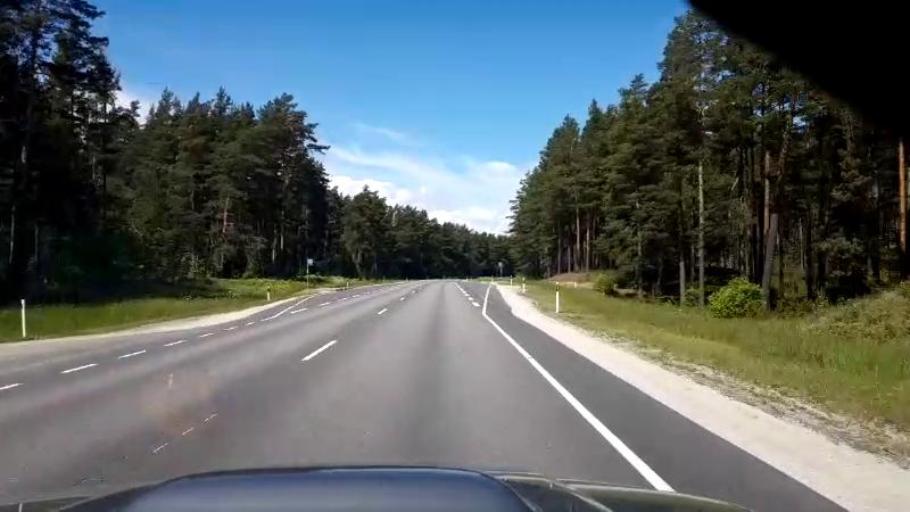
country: EE
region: Paernumaa
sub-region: Paernu linn
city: Parnu
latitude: 58.1487
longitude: 24.5008
